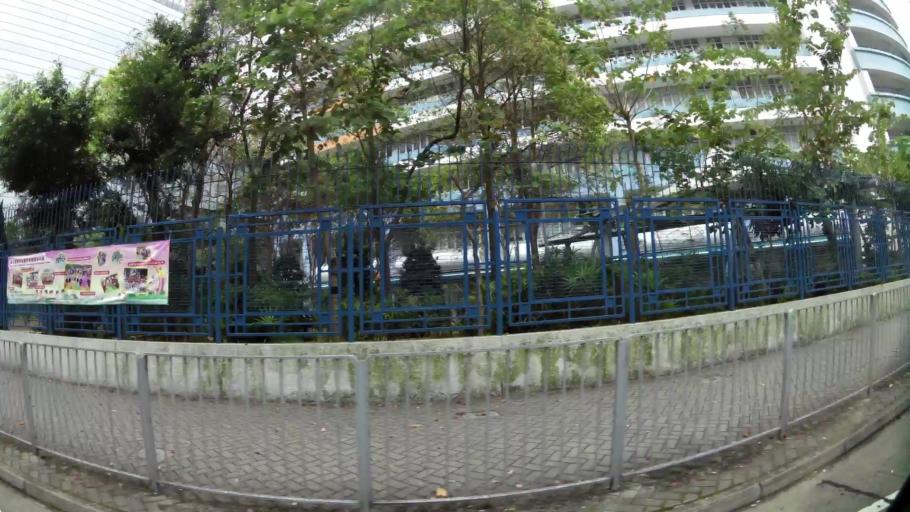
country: HK
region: Kowloon City
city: Kowloon
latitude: 22.3105
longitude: 114.2376
